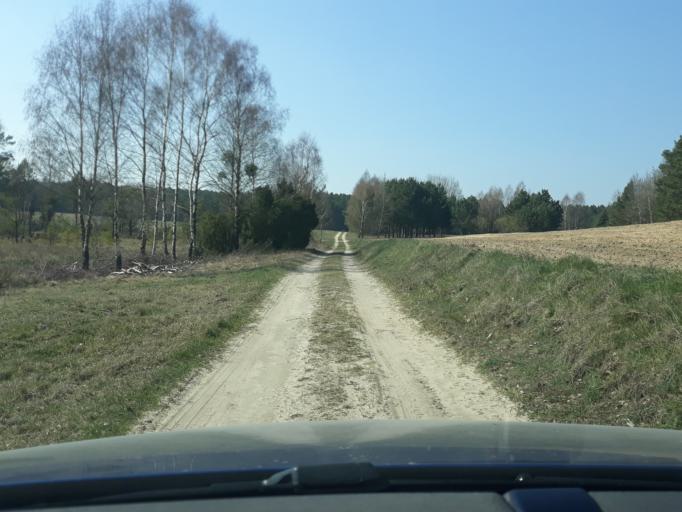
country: PL
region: Pomeranian Voivodeship
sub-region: Powiat bytowski
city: Lipnica
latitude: 53.8602
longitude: 17.4366
